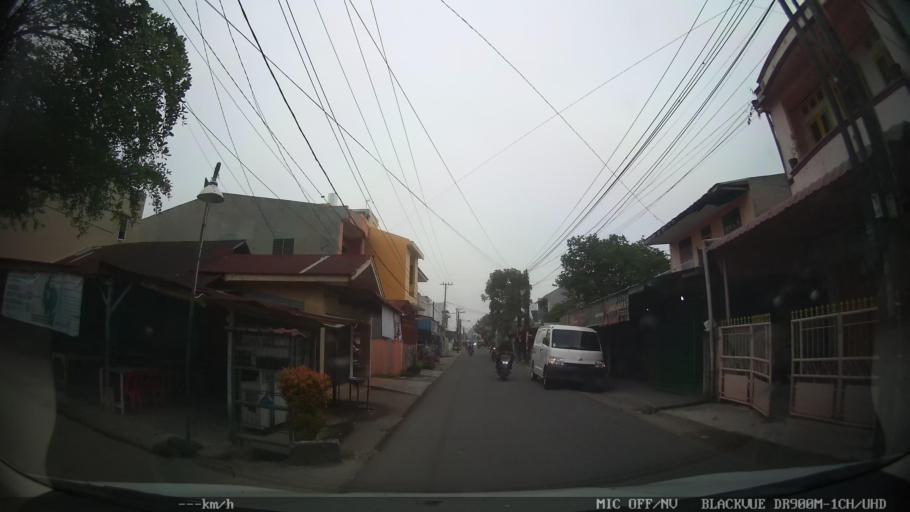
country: ID
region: North Sumatra
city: Deli Tua
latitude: 3.5435
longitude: 98.7064
